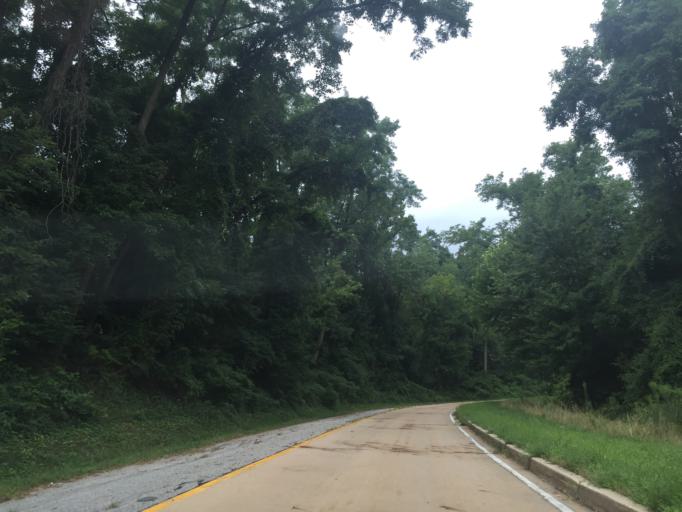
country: US
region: Maryland
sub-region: Baltimore County
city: Woodlawn
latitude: 39.3000
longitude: -76.7136
